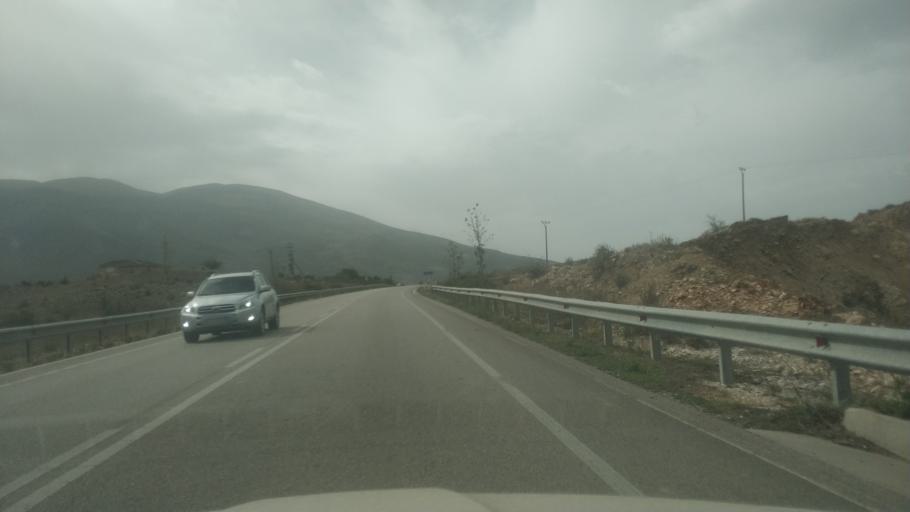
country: AL
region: Gjirokaster
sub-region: Rrethi i Tepelenes
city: Memaliaj
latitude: 40.3557
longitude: 19.9411
